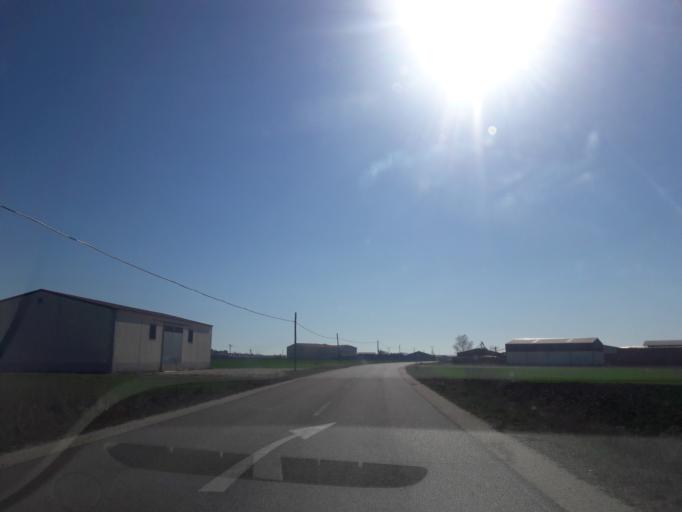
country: ES
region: Castille and Leon
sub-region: Provincia de Salamanca
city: Macotera
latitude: 40.8344
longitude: -5.2985
